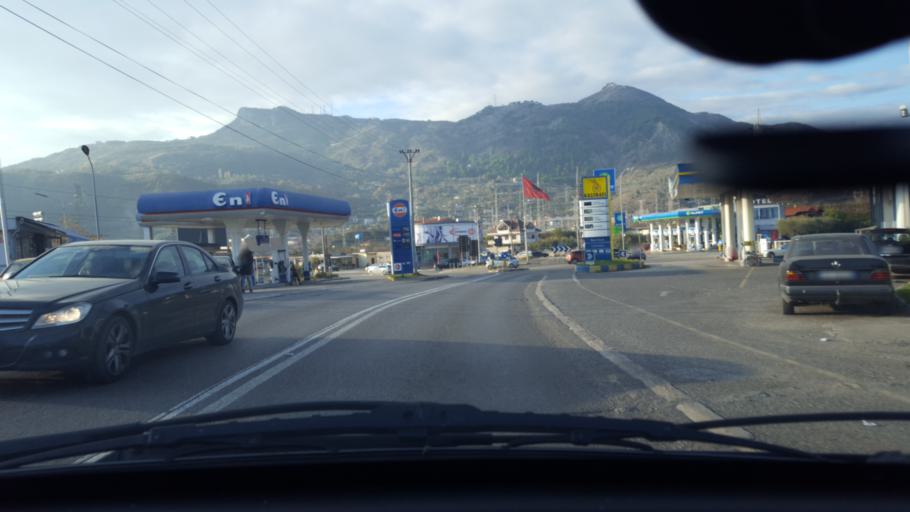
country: AL
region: Elbasan
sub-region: Rrethi i Elbasanit
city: Bradashesh
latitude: 41.0999
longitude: 20.0306
